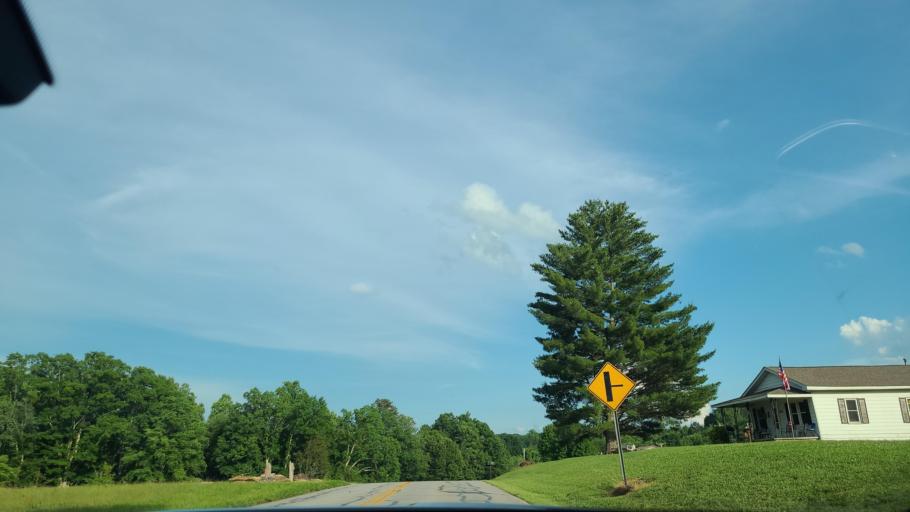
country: US
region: Kentucky
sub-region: Whitley County
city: Corbin
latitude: 36.8859
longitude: -84.2138
